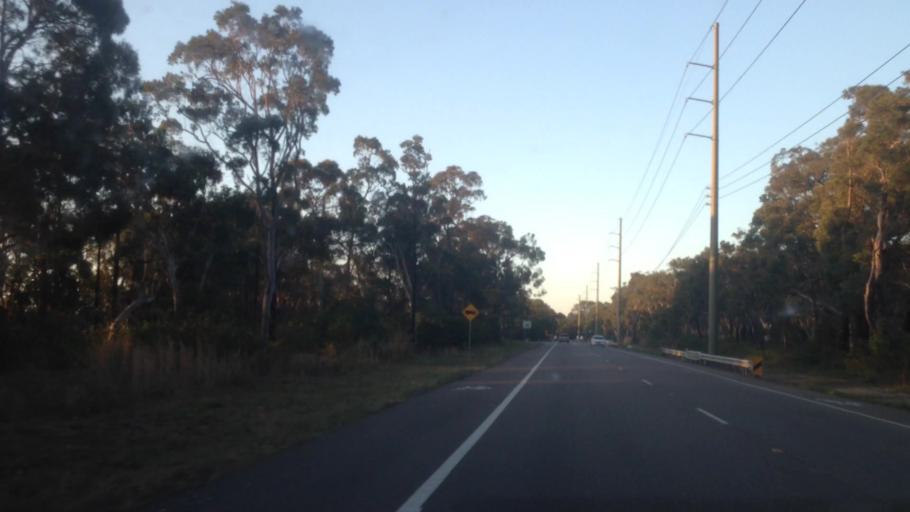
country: AU
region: New South Wales
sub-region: Wyong Shire
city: Kingfisher Shores
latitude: -33.1816
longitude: 151.5385
